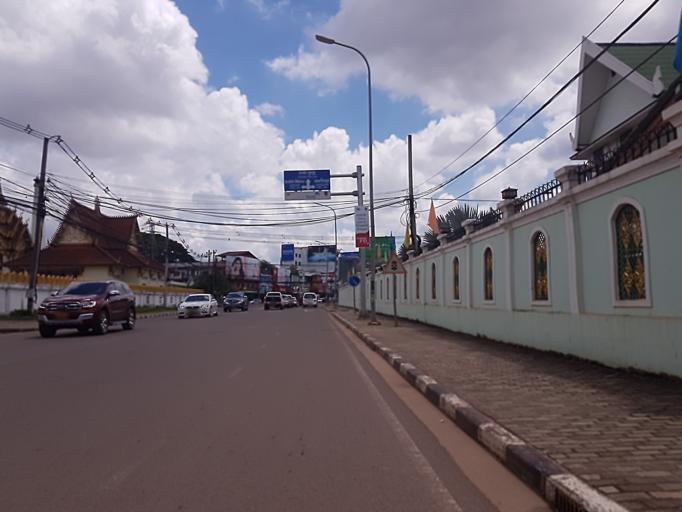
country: LA
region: Vientiane
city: Vientiane
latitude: 17.9673
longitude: 102.6165
